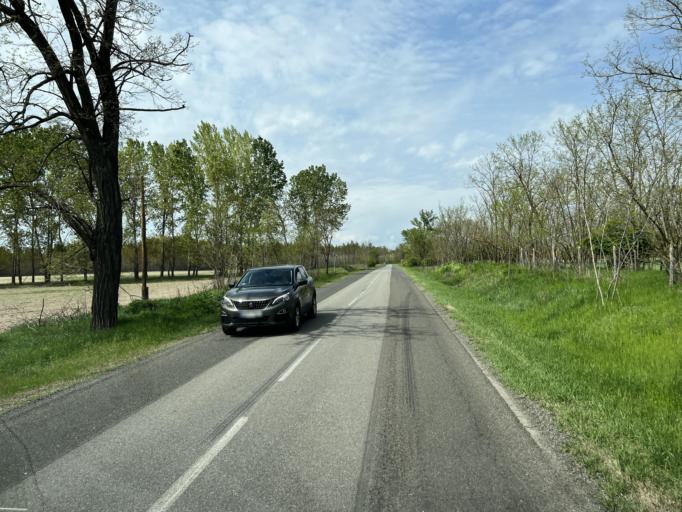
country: HU
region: Pest
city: Albertirsa
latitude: 47.1652
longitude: 19.6165
